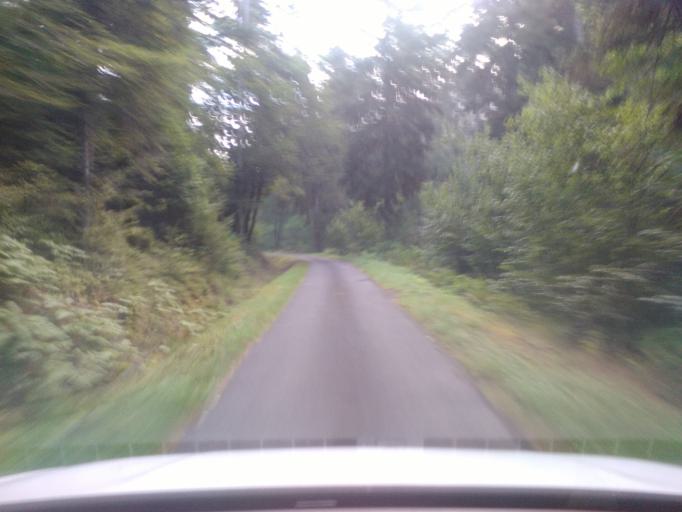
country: FR
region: Lorraine
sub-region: Departement des Vosges
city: Senones
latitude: 48.4165
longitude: 6.9333
